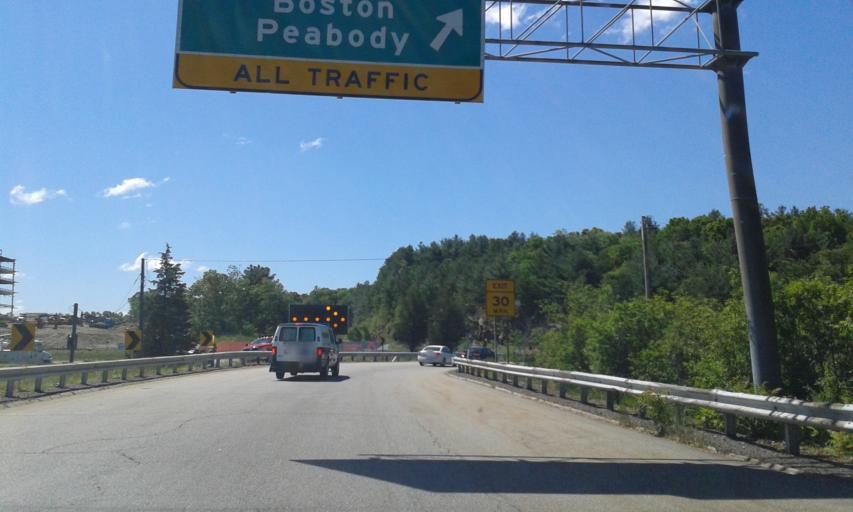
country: US
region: Massachusetts
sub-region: Middlesex County
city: Lexington
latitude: 42.4756
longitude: -71.2197
